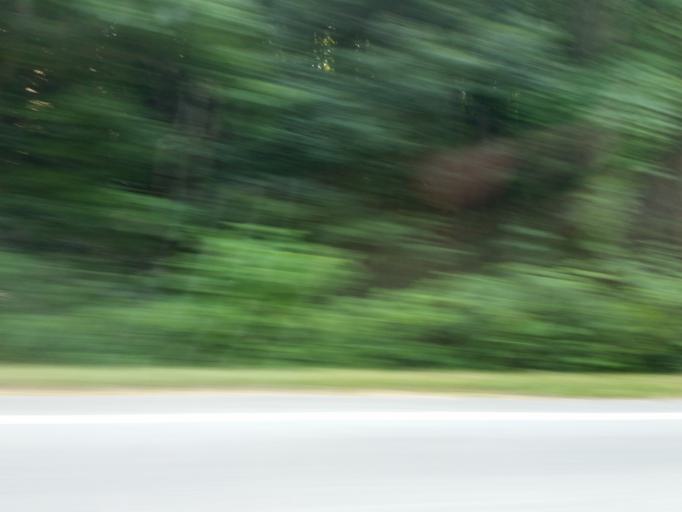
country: US
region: Tennessee
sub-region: Maury County
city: Mount Pleasant
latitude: 35.5746
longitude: -87.3229
